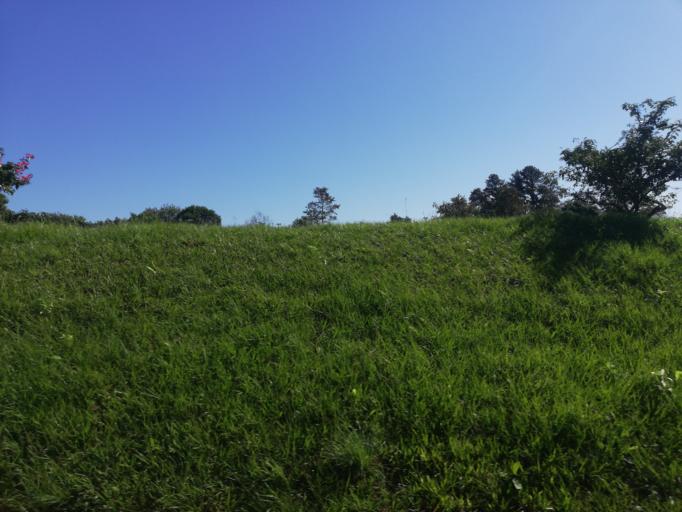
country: AR
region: Misiones
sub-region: Departamento de Iguazu
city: Puerto Iguazu
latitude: -25.5795
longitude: -54.5593
